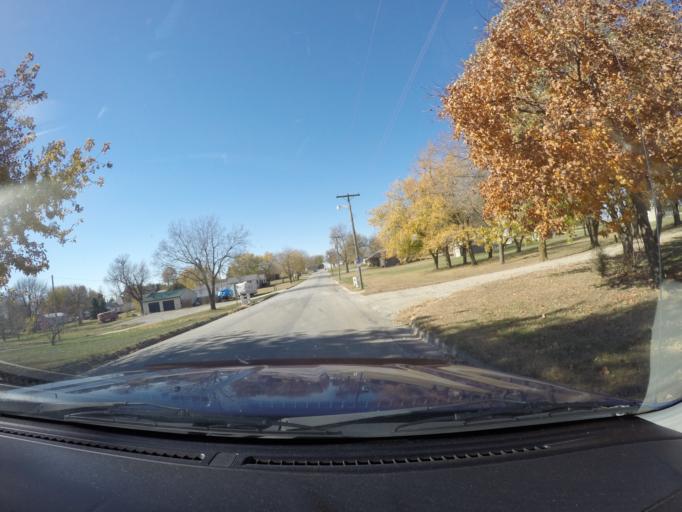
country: US
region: Kansas
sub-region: Nemaha County
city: Seneca
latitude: 39.8726
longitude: -96.2616
